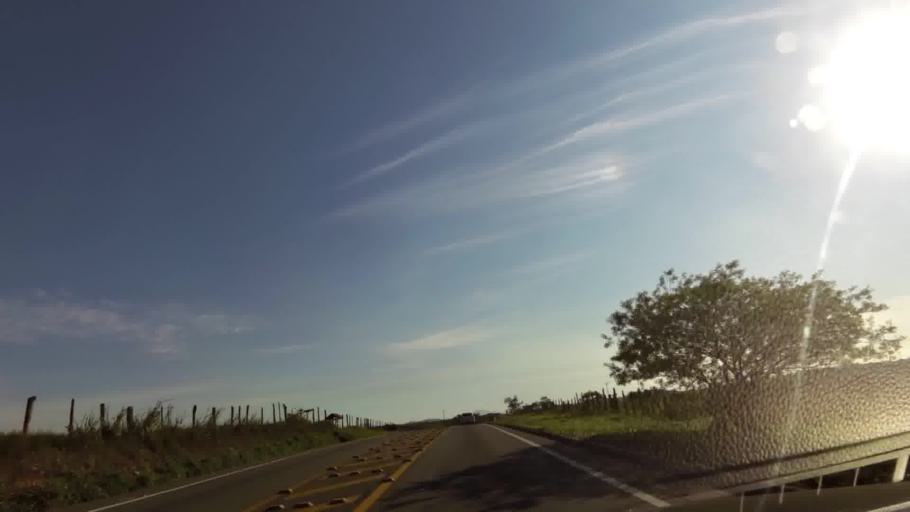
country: BR
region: Espirito Santo
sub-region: Viana
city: Viana
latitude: -20.4857
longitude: -40.4762
